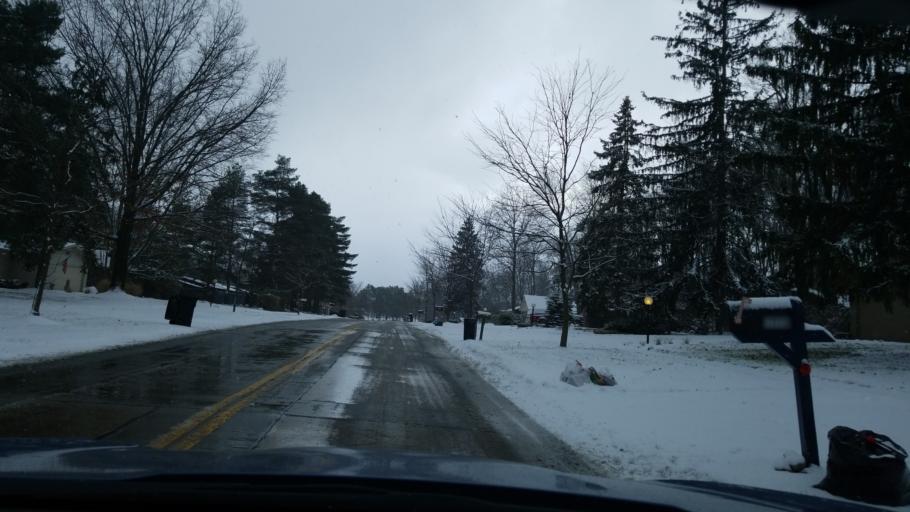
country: US
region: Ohio
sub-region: Cuyahoga County
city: Strongsville
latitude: 41.3196
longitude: -81.8210
